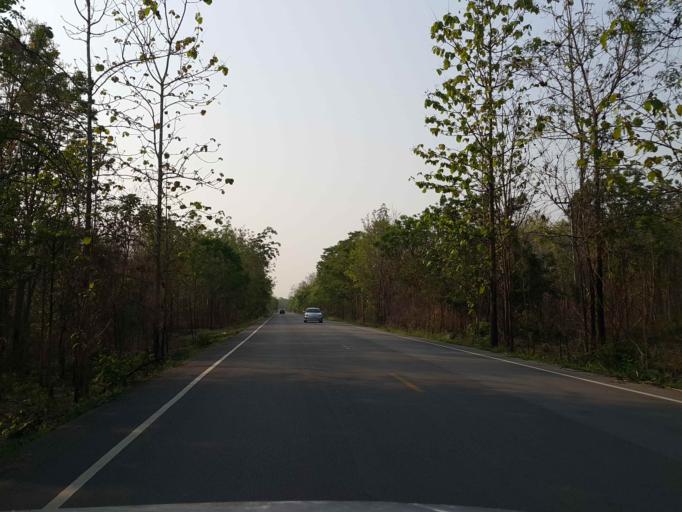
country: TH
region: Sukhothai
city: Thung Saliam
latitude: 17.3700
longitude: 99.4058
